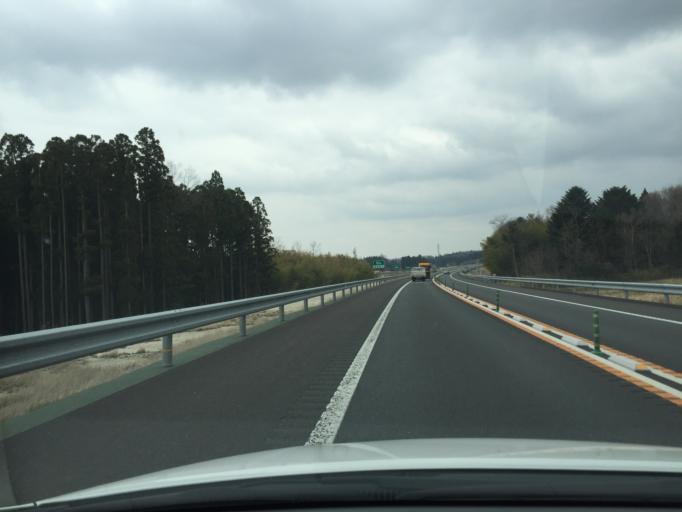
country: JP
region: Miyagi
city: Marumori
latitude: 37.8089
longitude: 140.8833
